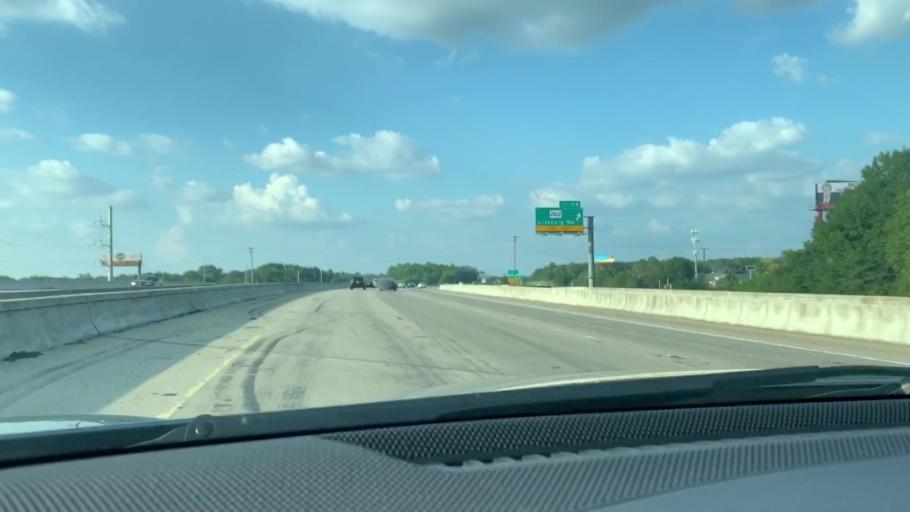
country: US
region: South Carolina
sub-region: Richland County
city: Forest Acres
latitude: 33.9735
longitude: -80.9549
